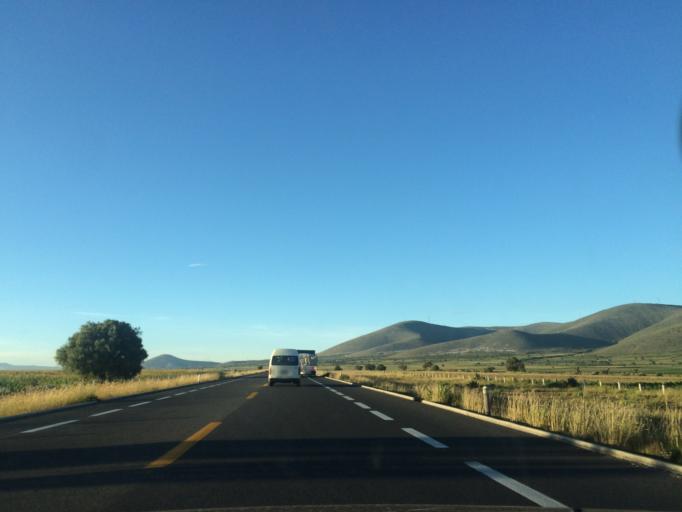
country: MX
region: Puebla
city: Morelos Canada
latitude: 18.7561
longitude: -97.4814
